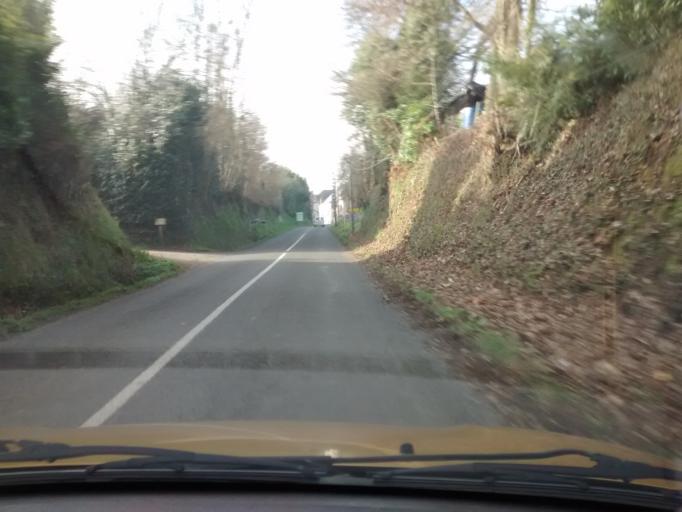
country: FR
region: Pays de la Loire
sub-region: Departement de la Loire-Atlantique
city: Vigneux-de-Bretagne
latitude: 47.3286
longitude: -1.7369
